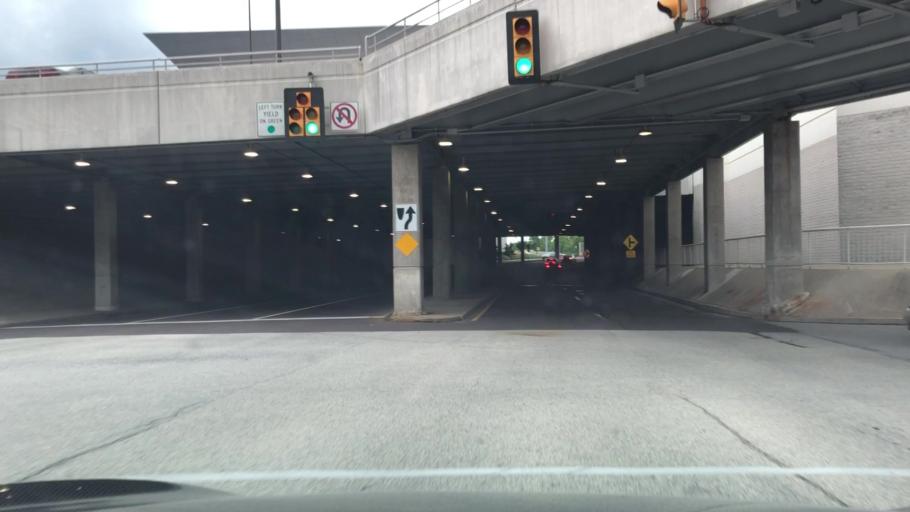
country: US
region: Pennsylvania
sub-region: Montgomery County
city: King of Prussia
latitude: 40.0878
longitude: -75.3879
